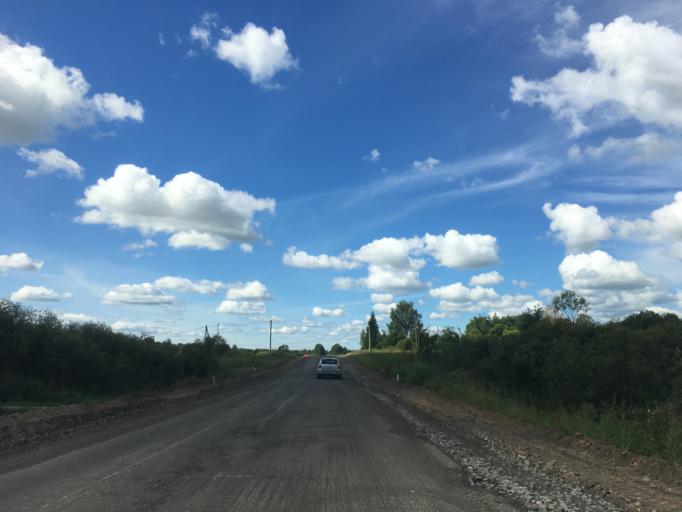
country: RU
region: Pskov
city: Palkino
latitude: 57.5513
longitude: 28.0495
